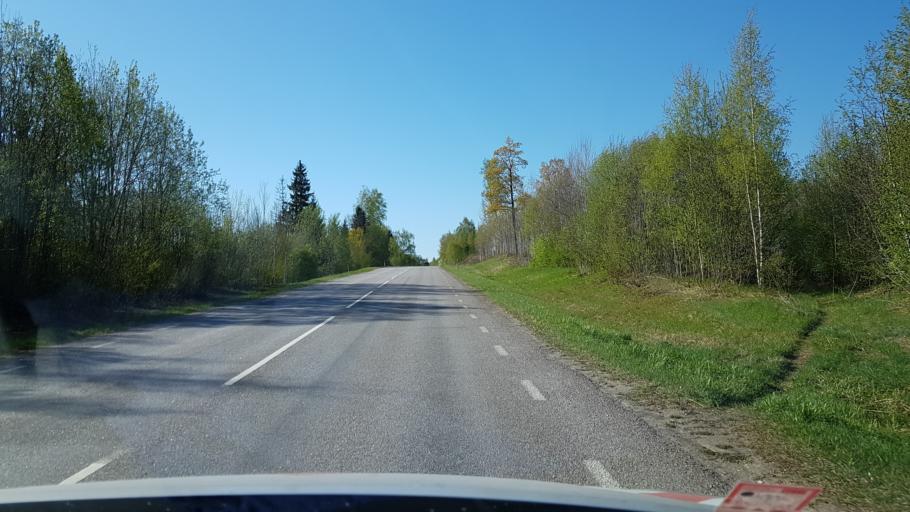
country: EE
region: Vorumaa
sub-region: Voru linn
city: Voru
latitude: 57.7902
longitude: 27.0344
